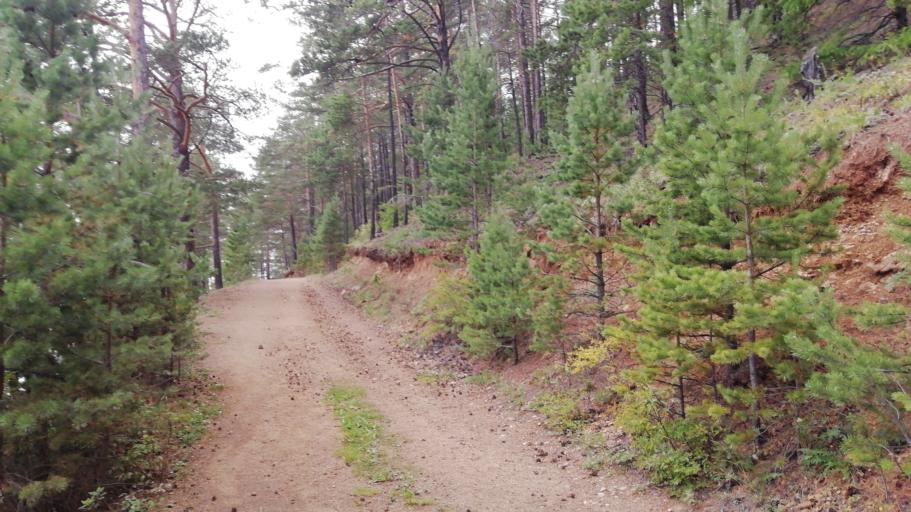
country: RU
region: Irkutsk
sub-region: Irkutskiy Rayon
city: Listvyanka
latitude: 51.8930
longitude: 105.0472
